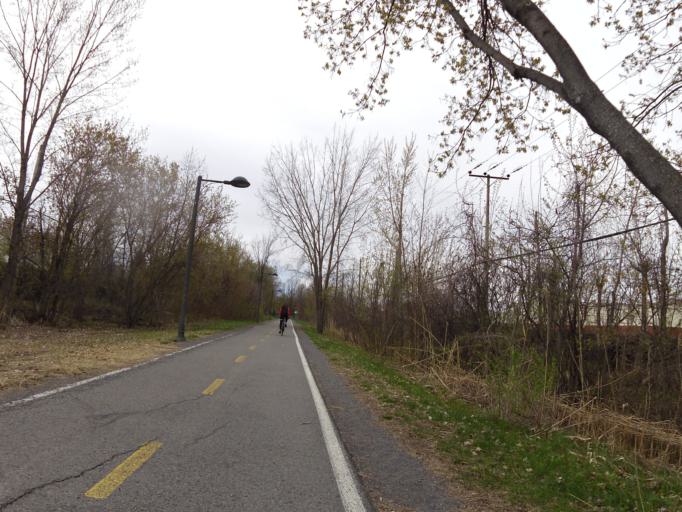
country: CA
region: Quebec
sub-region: Laurentides
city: Sainte-Marthe-sur-le-Lac
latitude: 45.5373
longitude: -73.9225
